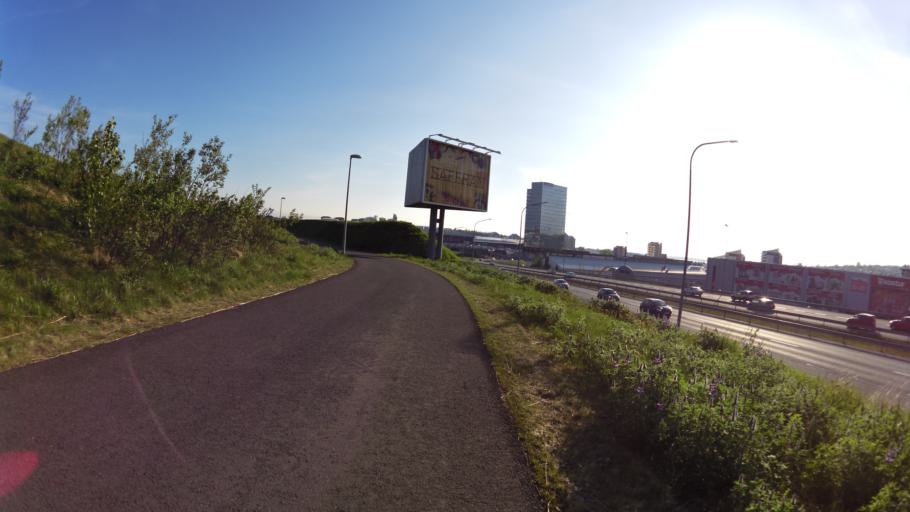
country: IS
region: Capital Region
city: Reykjavik
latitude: 64.1039
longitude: -21.8703
